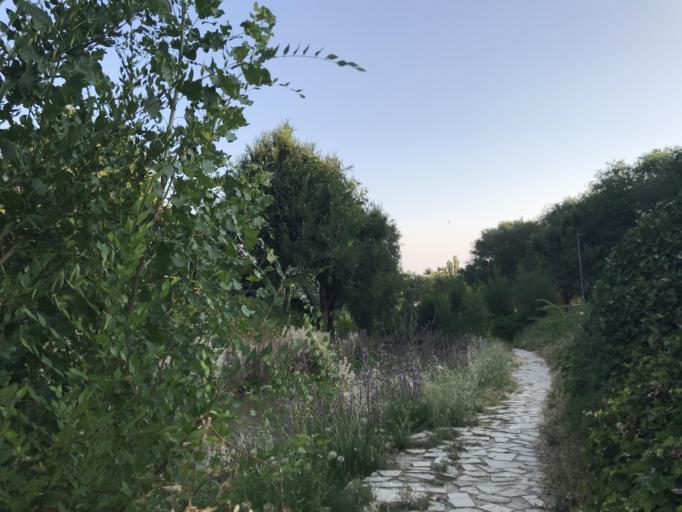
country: ES
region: Castille and Leon
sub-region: Provincia de Valladolid
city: Valladolid
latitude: 41.6566
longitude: -4.7111
